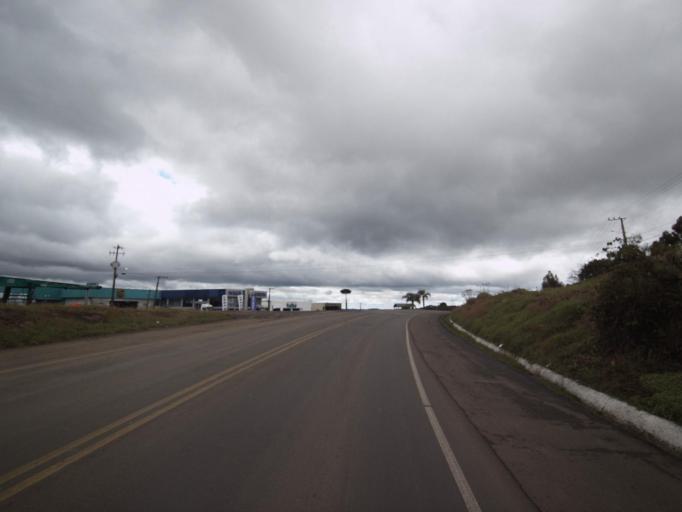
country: BR
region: Santa Catarina
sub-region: Concordia
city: Concordia
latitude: -27.2429
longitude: -51.9515
